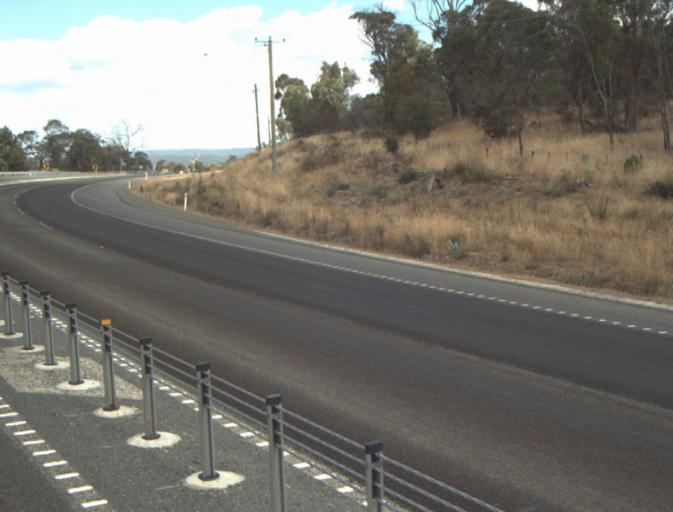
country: AU
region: Tasmania
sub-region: Launceston
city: Mayfield
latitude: -41.2965
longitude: 147.0496
